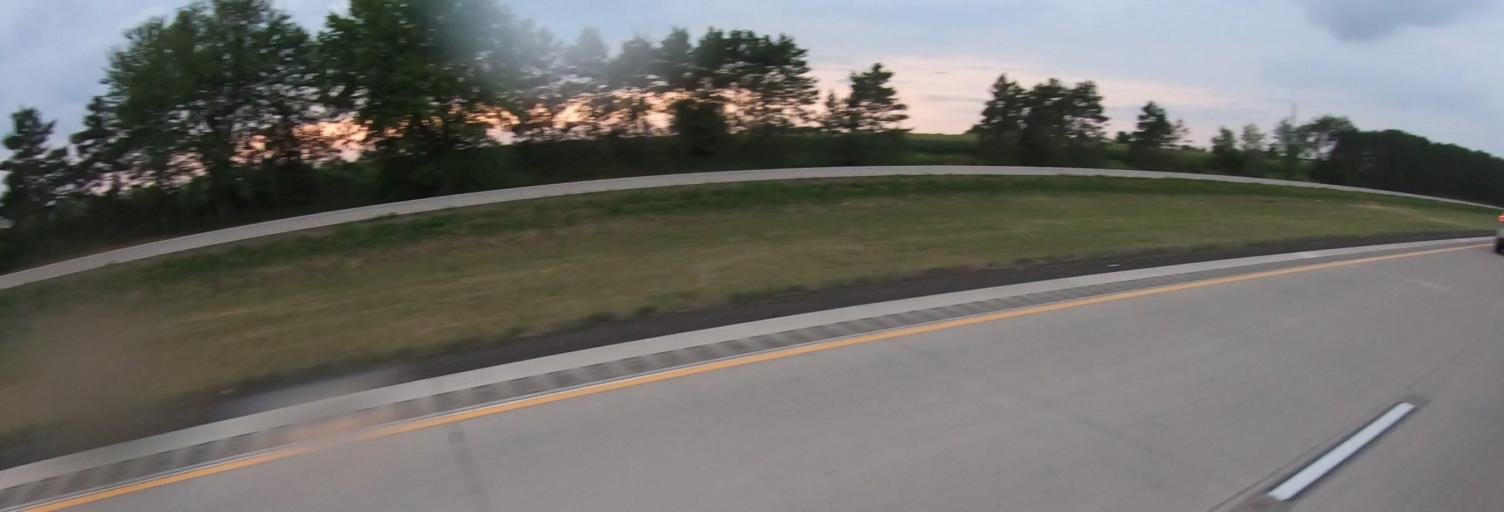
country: US
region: Minnesota
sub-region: Pine County
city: Pine City
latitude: 45.8052
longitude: -92.9896
